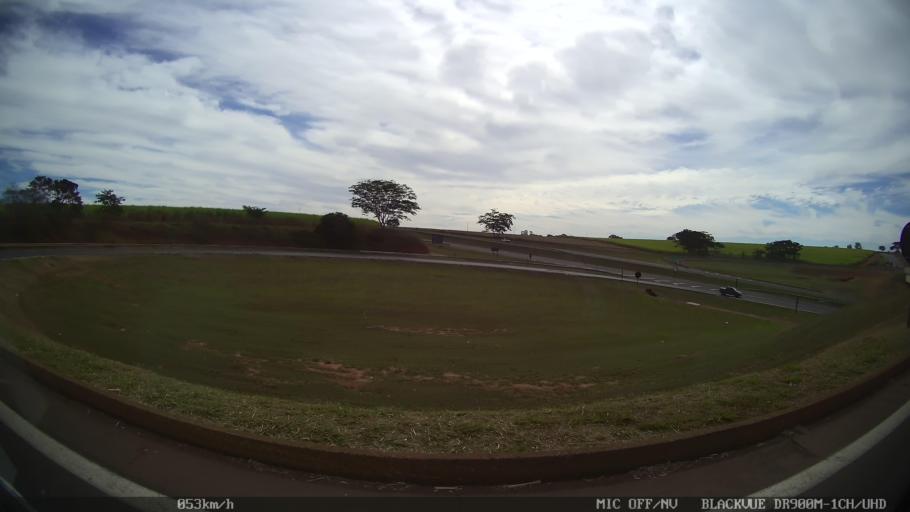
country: BR
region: Sao Paulo
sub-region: Taquaritinga
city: Taquaritinga
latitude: -21.5158
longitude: -48.5422
